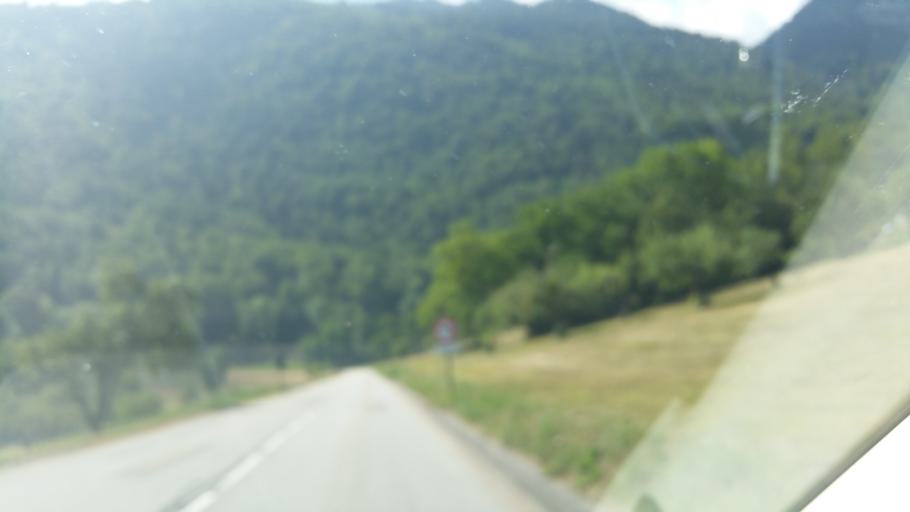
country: FR
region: Rhone-Alpes
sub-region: Departement de la Savoie
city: Aigueblanche
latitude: 45.4930
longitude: 6.5017
